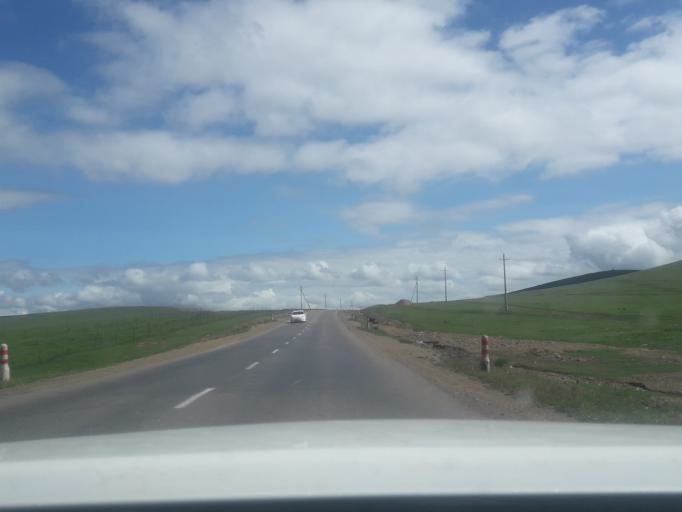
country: MN
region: Central Aimak
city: Altanbulag
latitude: 47.9012
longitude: 106.4910
